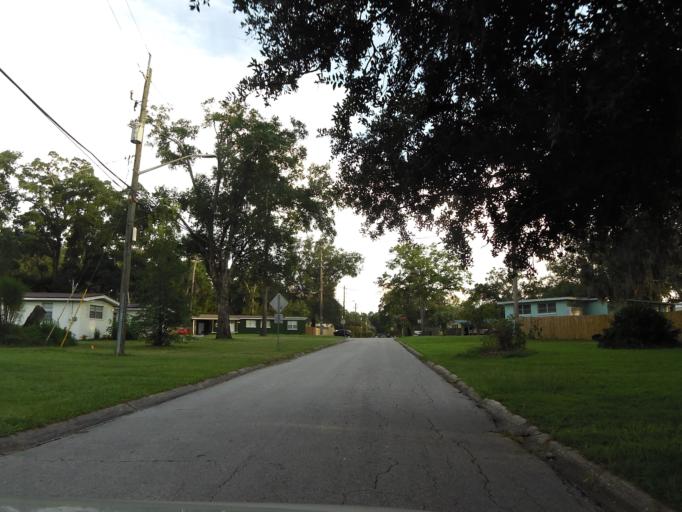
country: US
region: Florida
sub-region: Clay County
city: Orange Park
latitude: 30.2159
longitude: -81.7069
